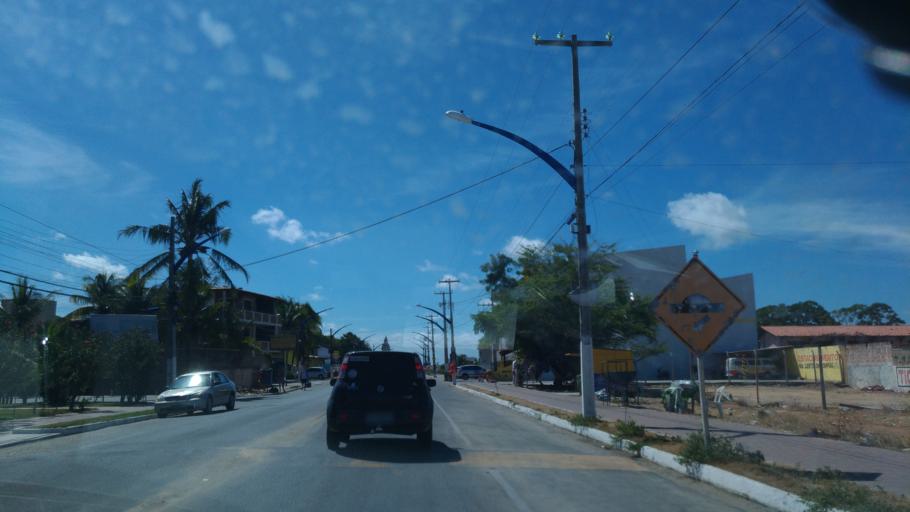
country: BR
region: Alagoas
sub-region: Marechal Deodoro
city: Marechal Deodoro
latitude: -9.7692
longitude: -35.8458
